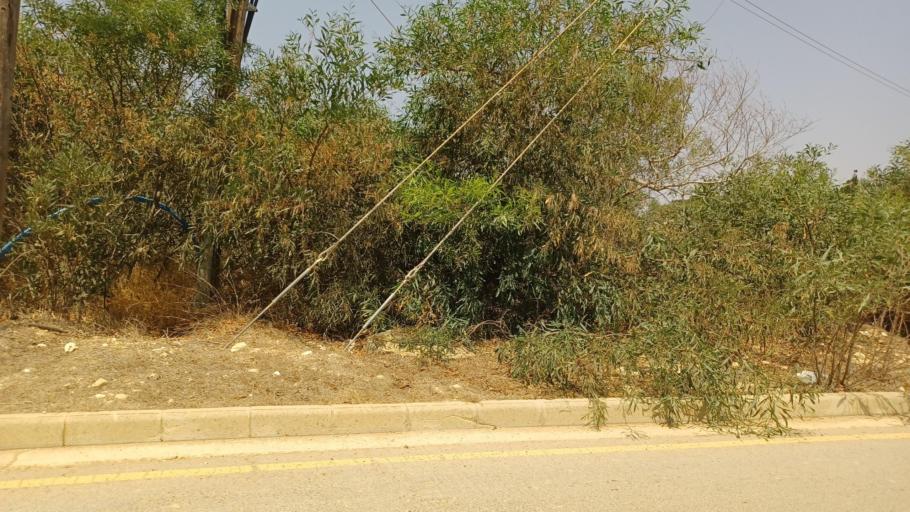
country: CY
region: Ammochostos
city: Ayia Napa
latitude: 34.9817
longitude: 34.0233
